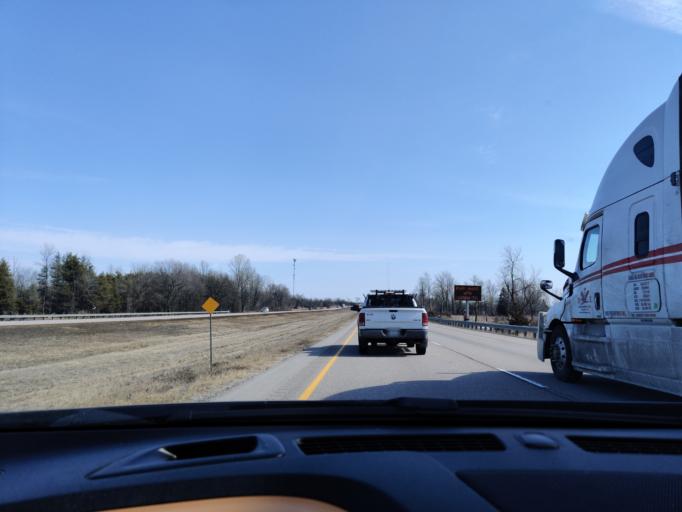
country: CA
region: Ontario
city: Kingston
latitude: 44.2862
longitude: -76.6419
